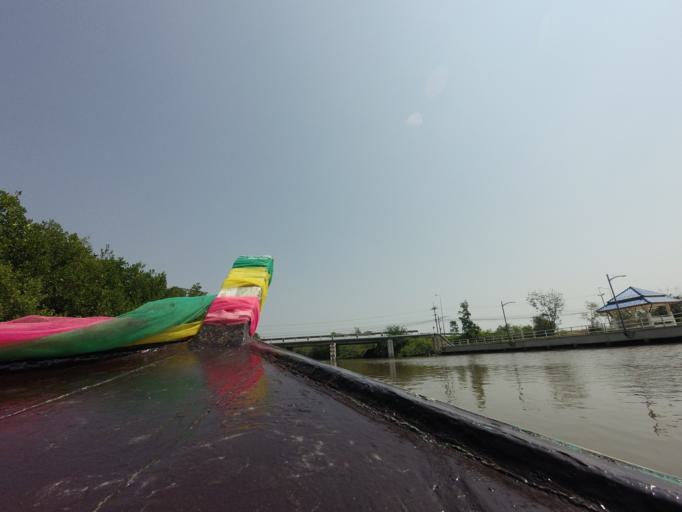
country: TH
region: Prachuap Khiri Khan
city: Kui Buri
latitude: 12.1341
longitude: 99.9633
